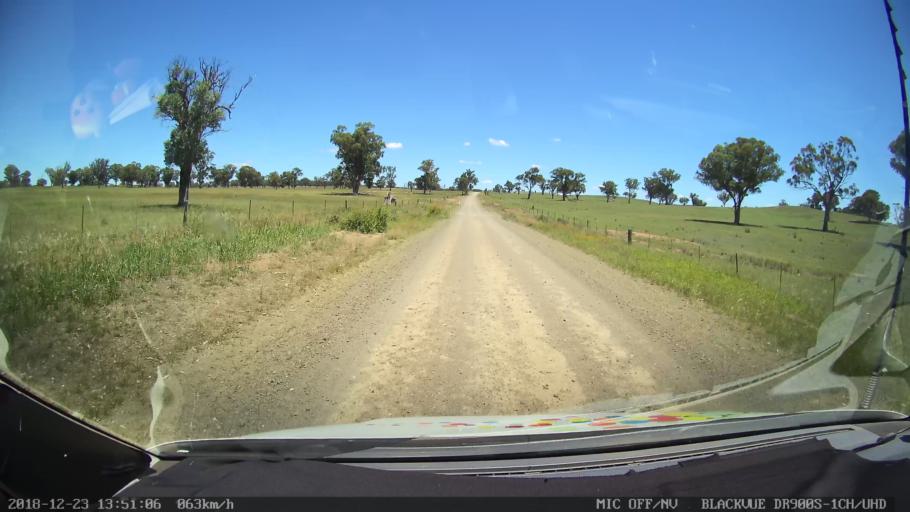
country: AU
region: New South Wales
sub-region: Tamworth Municipality
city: Manilla
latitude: -30.5366
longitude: 151.1056
